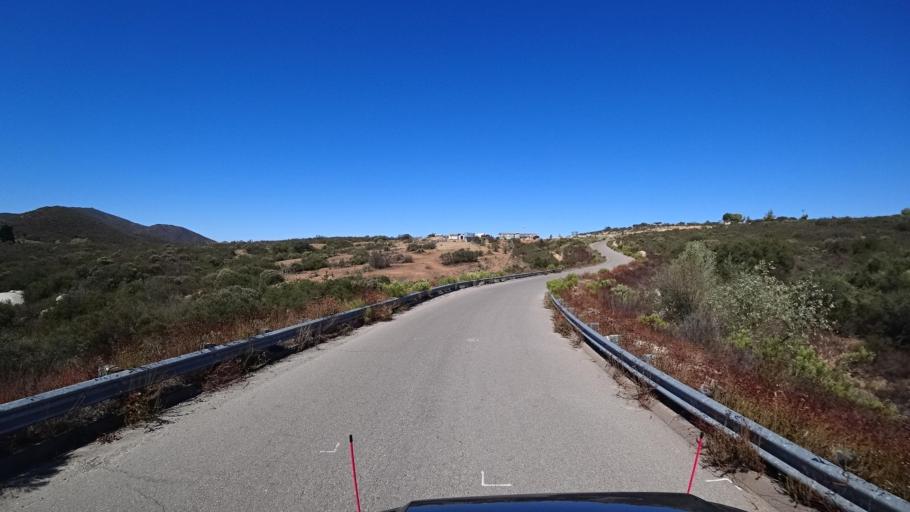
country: US
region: California
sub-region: San Diego County
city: Alpine
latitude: 32.7596
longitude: -116.7725
